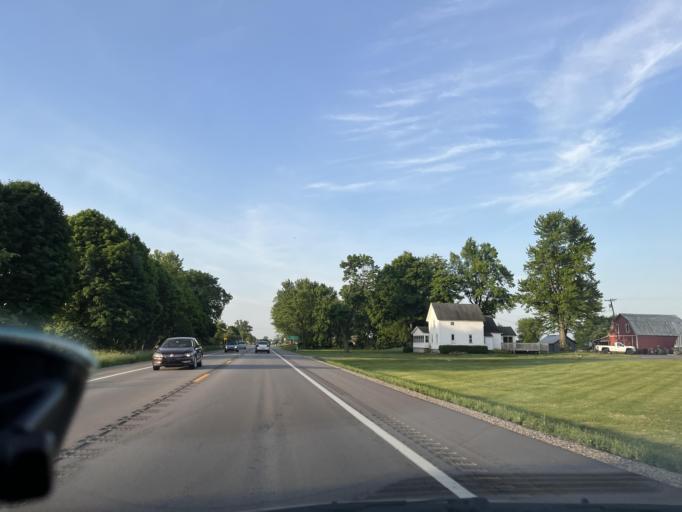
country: US
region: Michigan
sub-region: Kent County
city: Caledonia
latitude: 42.7718
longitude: -85.5066
